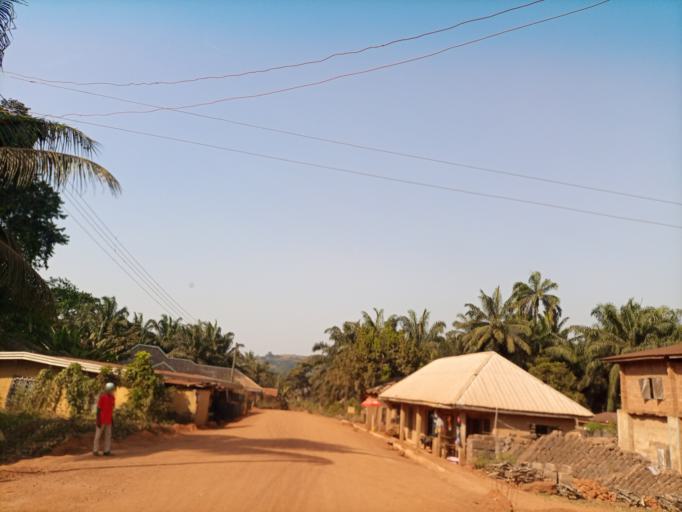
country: NG
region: Enugu
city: Aku
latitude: 6.6975
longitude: 7.3264
